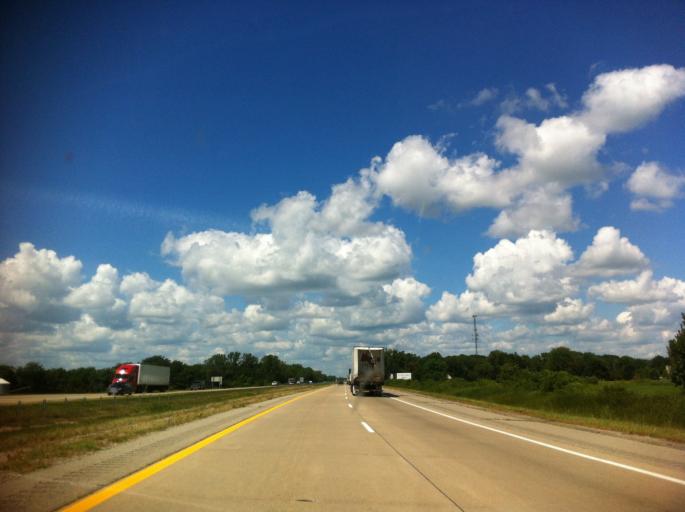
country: US
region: Michigan
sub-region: Monroe County
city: Dundee
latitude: 41.9753
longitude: -83.6783
